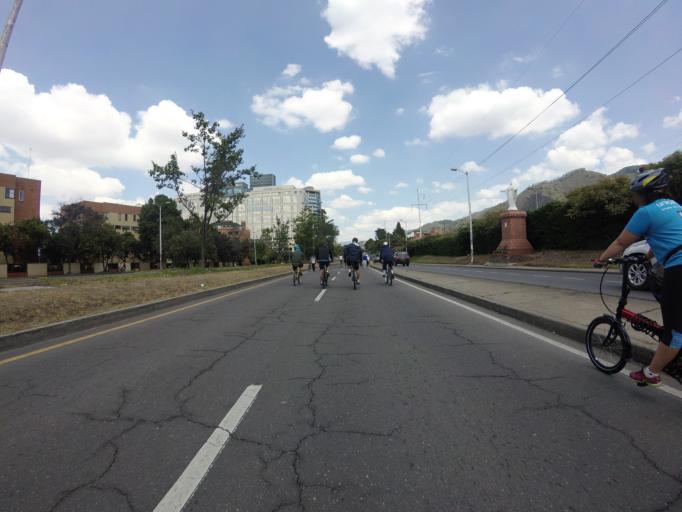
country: CO
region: Bogota D.C.
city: Barrio San Luis
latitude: 4.6893
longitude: -74.0346
